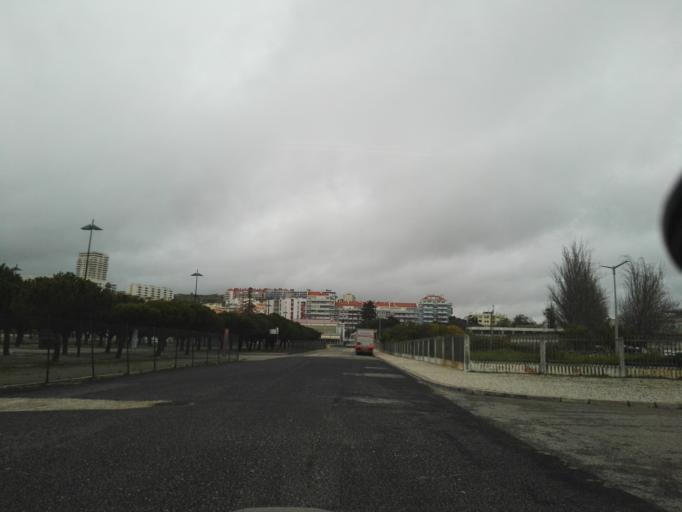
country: PT
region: Lisbon
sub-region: Oeiras
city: Alges
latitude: 38.6966
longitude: -9.2315
